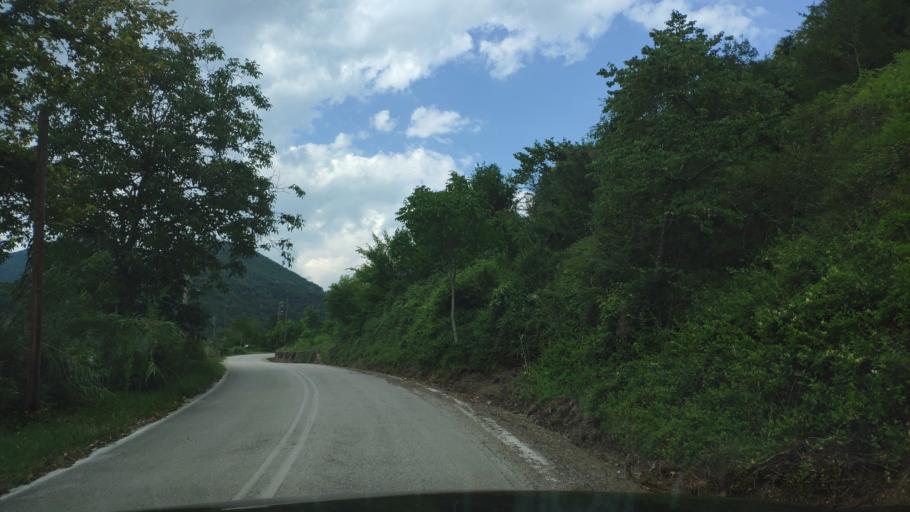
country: GR
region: Epirus
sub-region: Nomos Artas
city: Agios Dimitrios
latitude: 39.4570
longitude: 21.0348
